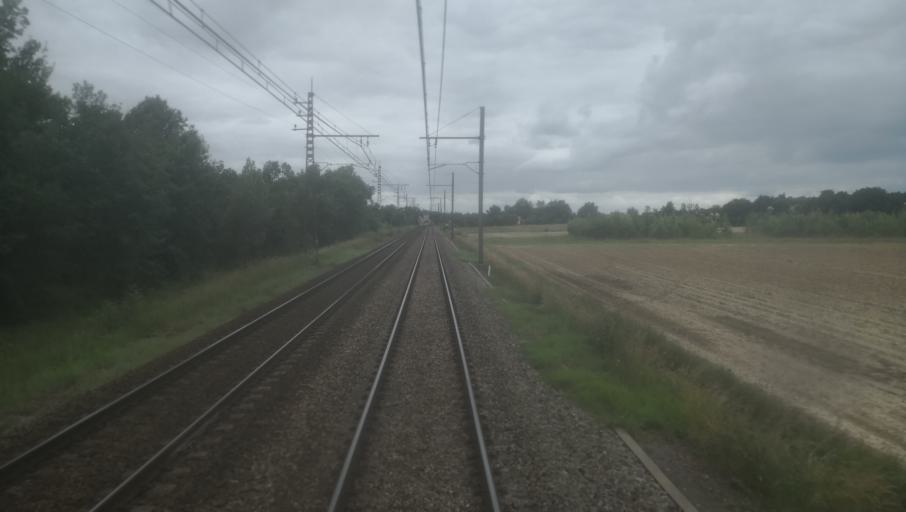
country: FR
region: Midi-Pyrenees
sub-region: Departement du Tarn-et-Garonne
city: Finhan
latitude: 43.9078
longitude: 1.2631
